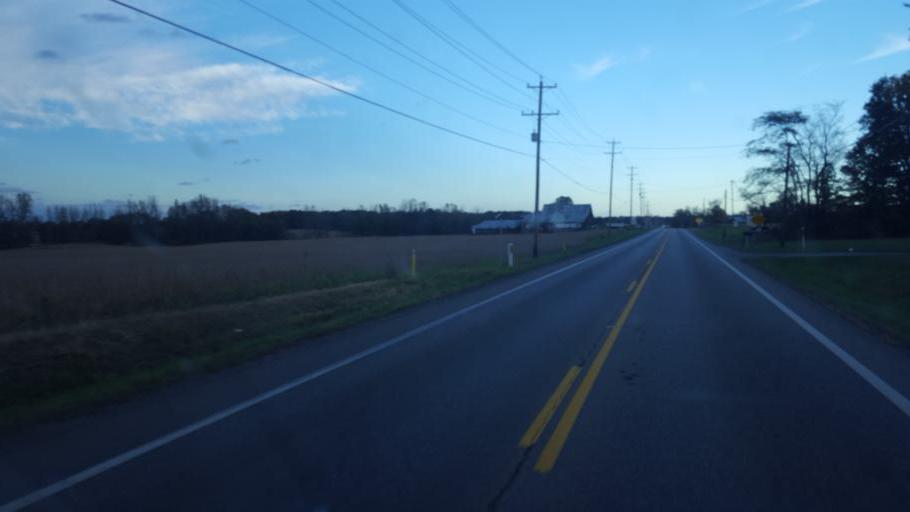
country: US
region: Ohio
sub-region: Licking County
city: Johnstown
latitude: 40.1417
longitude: -82.7138
